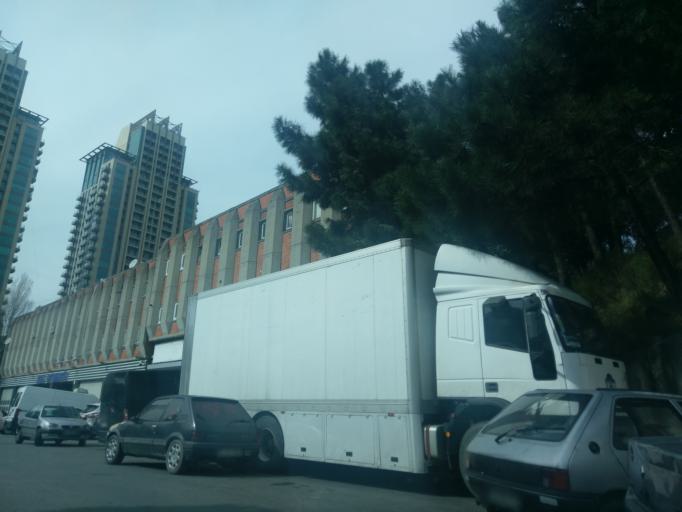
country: TR
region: Istanbul
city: Sisli
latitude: 41.1172
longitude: 29.0169
